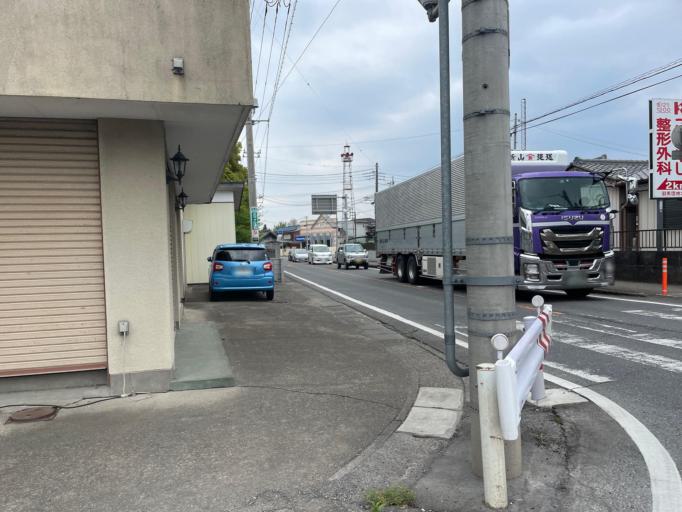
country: JP
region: Gunma
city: Isesaki
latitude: 36.2788
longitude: 139.2116
